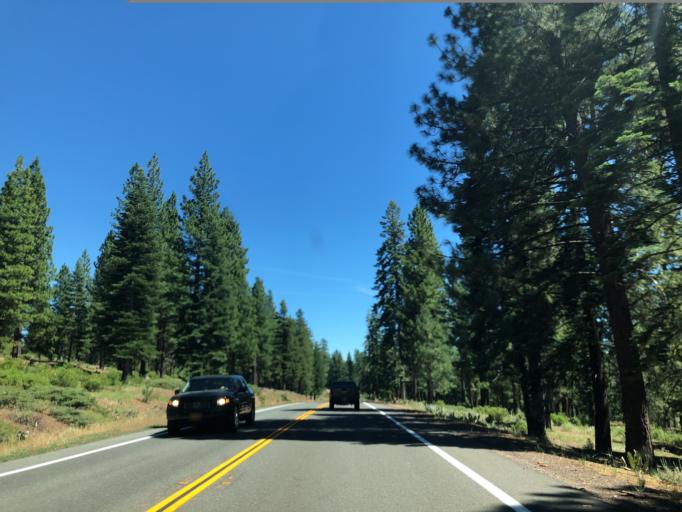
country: US
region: California
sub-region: Lassen County
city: Susanville
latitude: 40.4366
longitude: -120.8317
